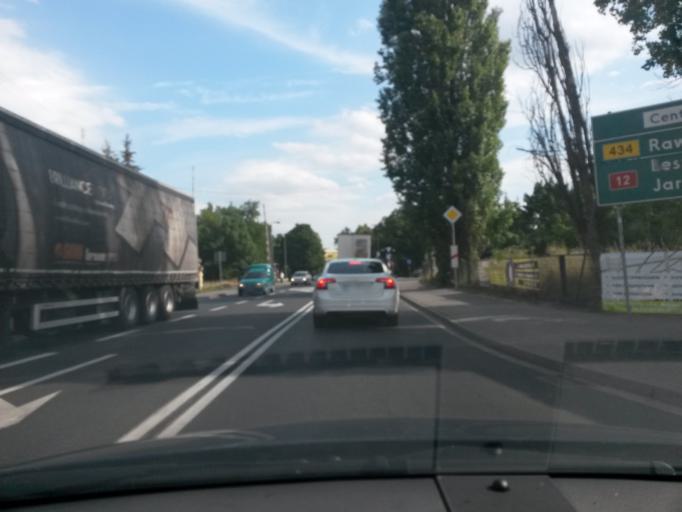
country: PL
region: Greater Poland Voivodeship
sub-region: Powiat gostynski
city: Gostyn
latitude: 51.8841
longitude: 17.0113
